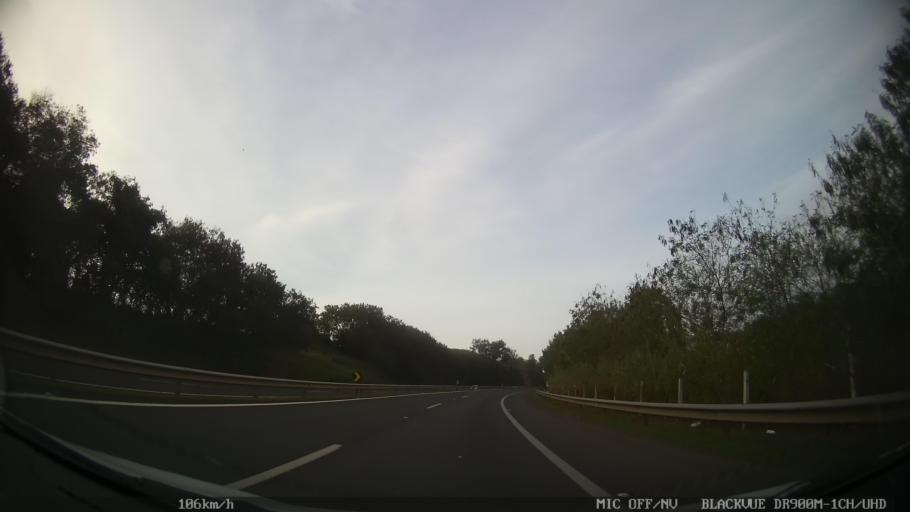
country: BR
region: Sao Paulo
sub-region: Piracicaba
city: Piracicaba
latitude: -22.6936
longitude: -47.5900
